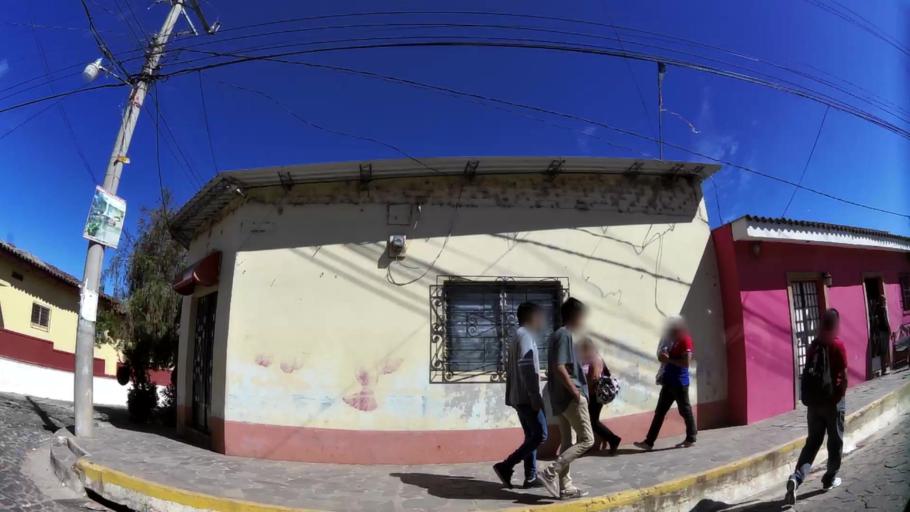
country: SV
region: Ahuachapan
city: Concepcion de Ataco
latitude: 13.8670
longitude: -89.8507
